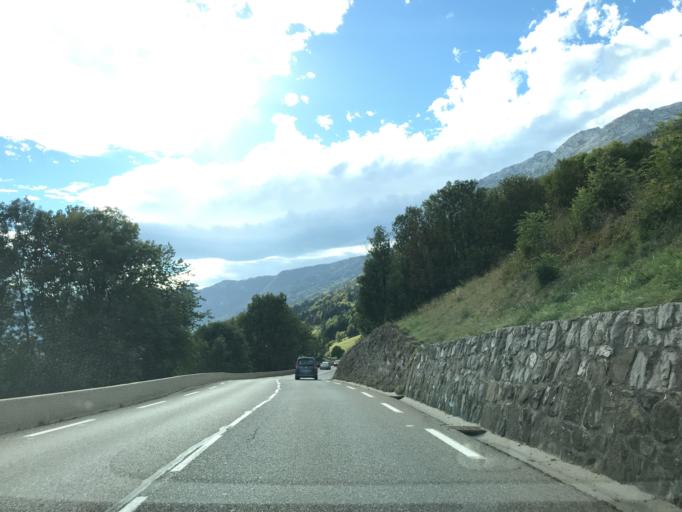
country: FR
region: Rhone-Alpes
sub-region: Departement de la Haute-Savoie
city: Saint-Jean-de-Sixt
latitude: 45.9206
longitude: 6.3913
